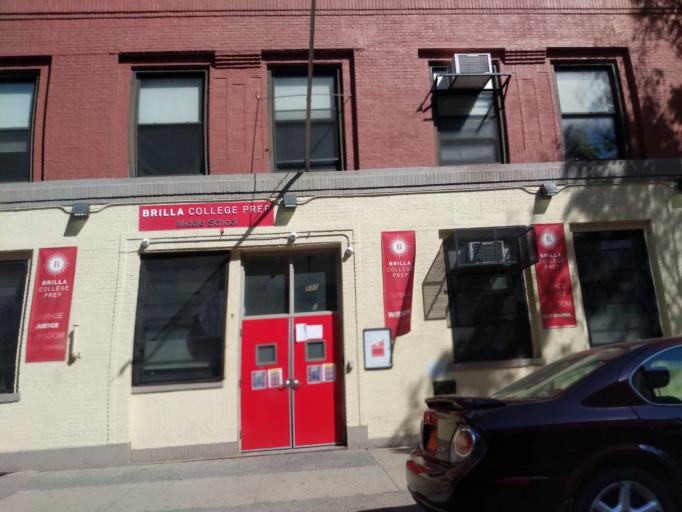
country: US
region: New York
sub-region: New York County
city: Inwood
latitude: 40.8154
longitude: -73.9200
